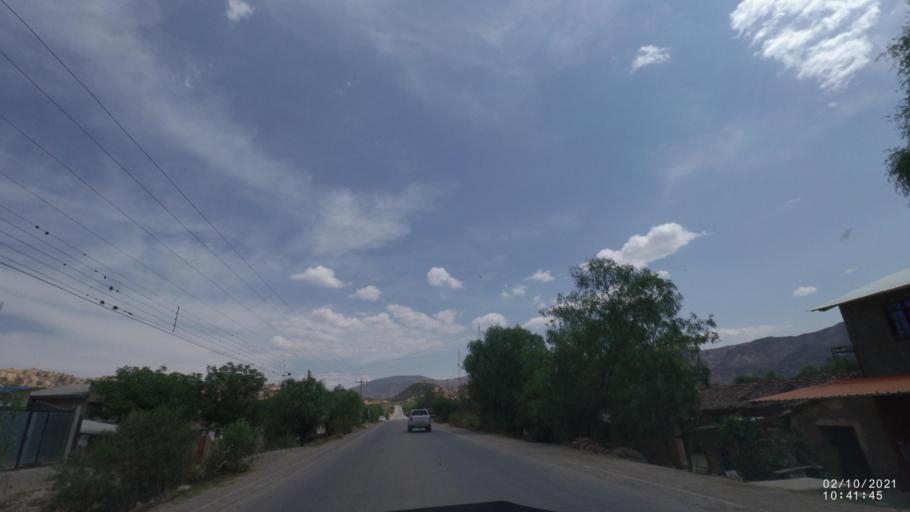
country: BO
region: Cochabamba
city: Capinota
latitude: -17.6118
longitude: -66.2921
